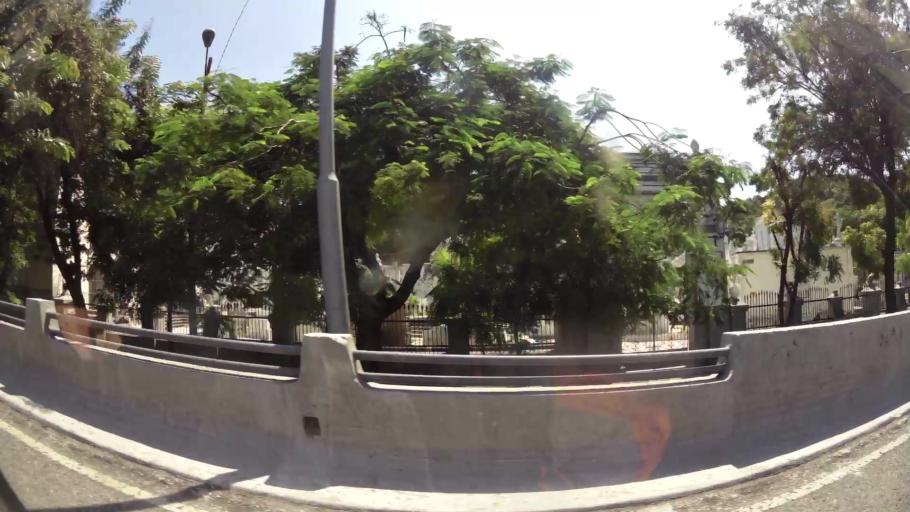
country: EC
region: Guayas
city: Guayaquil
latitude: -2.1834
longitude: -79.8869
